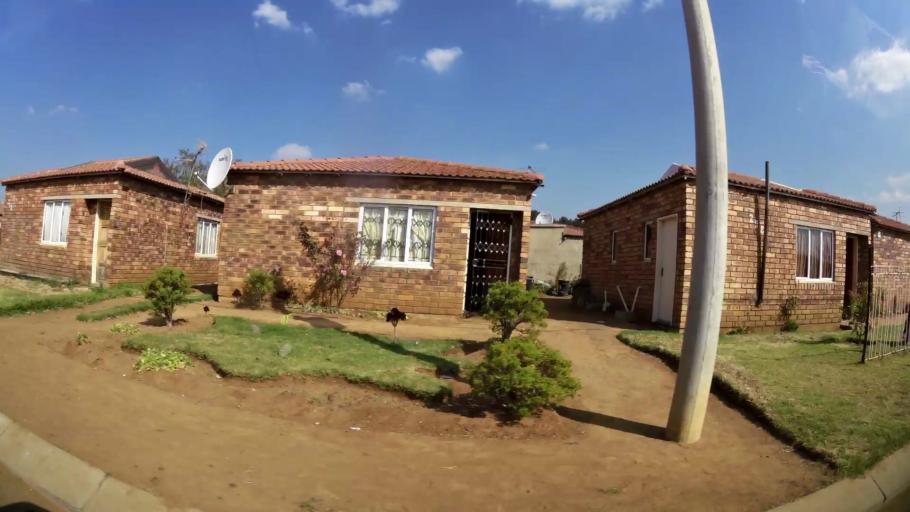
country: ZA
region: Gauteng
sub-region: Ekurhuleni Metropolitan Municipality
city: Benoni
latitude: -26.1369
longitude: 28.4090
